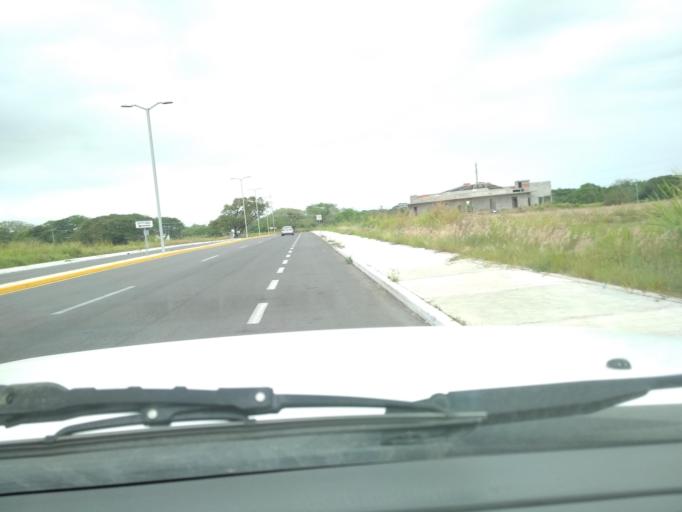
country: MX
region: Veracruz
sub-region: Alvarado
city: Playa de la Libertad
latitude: 19.0882
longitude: -96.1190
